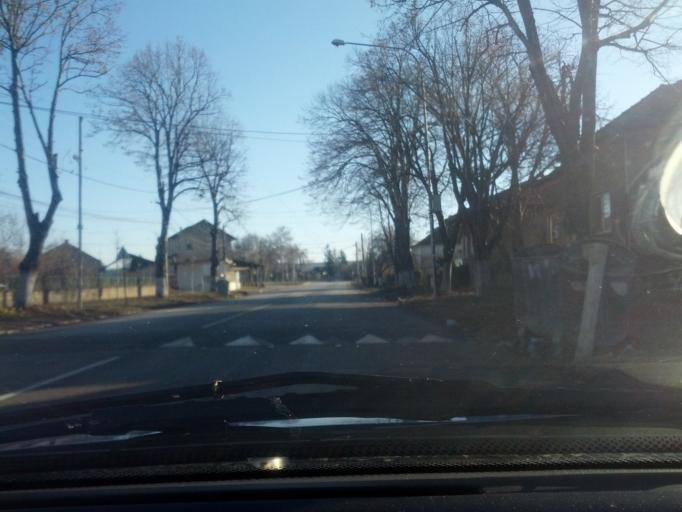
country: BG
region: Vratsa
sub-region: Obshtina Kozloduy
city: Kozloduy
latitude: 43.7641
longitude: 23.7410
